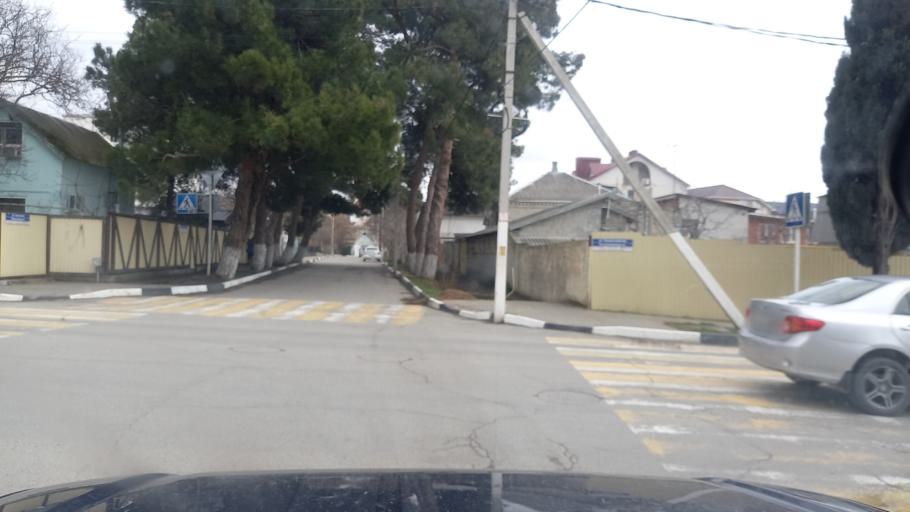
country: RU
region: Krasnodarskiy
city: Gelendzhik
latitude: 44.5594
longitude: 38.0873
